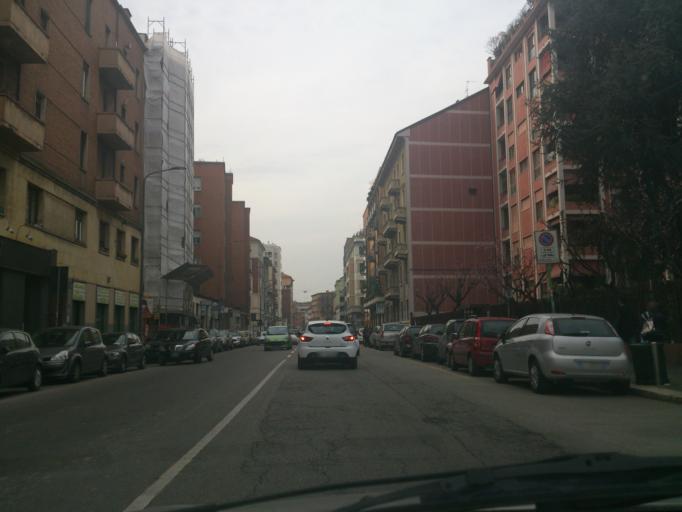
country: IT
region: Lombardy
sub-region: Citta metropolitana di Milano
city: Milano
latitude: 45.4559
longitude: 9.2165
